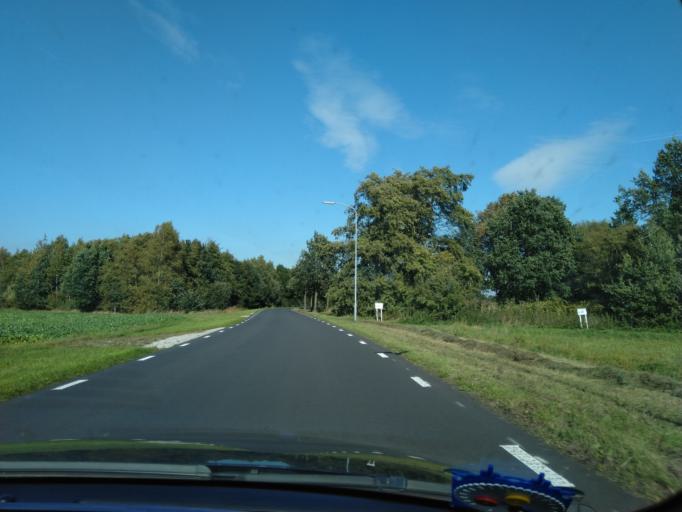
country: NL
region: Groningen
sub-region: Gemeente Hoogezand-Sappemeer
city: Sappemeer
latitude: 53.0847
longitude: 6.7878
